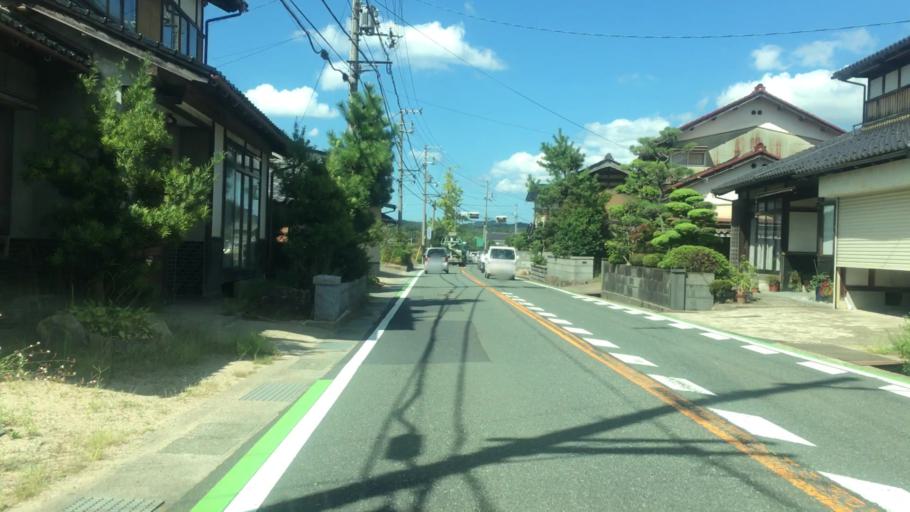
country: JP
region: Kyoto
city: Miyazu
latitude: 35.5887
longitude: 135.0384
